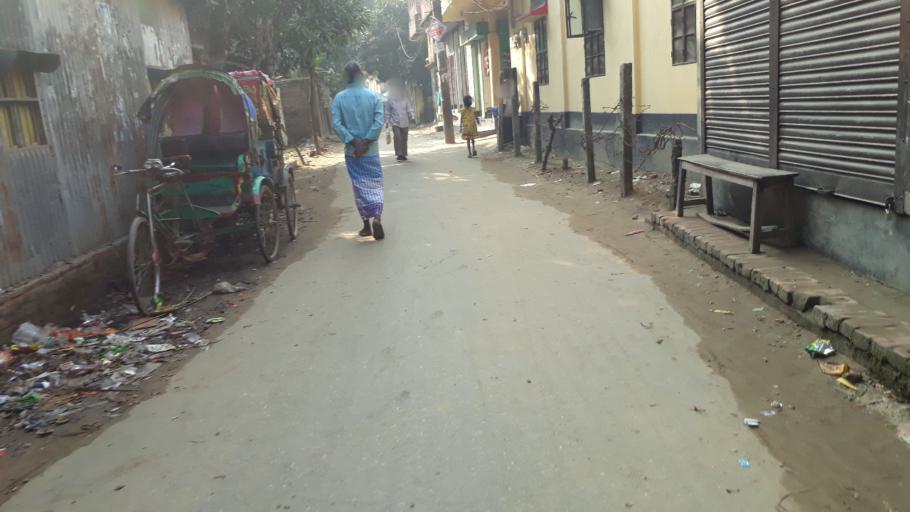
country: BD
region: Dhaka
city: Tungi
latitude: 23.8847
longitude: 90.2616
